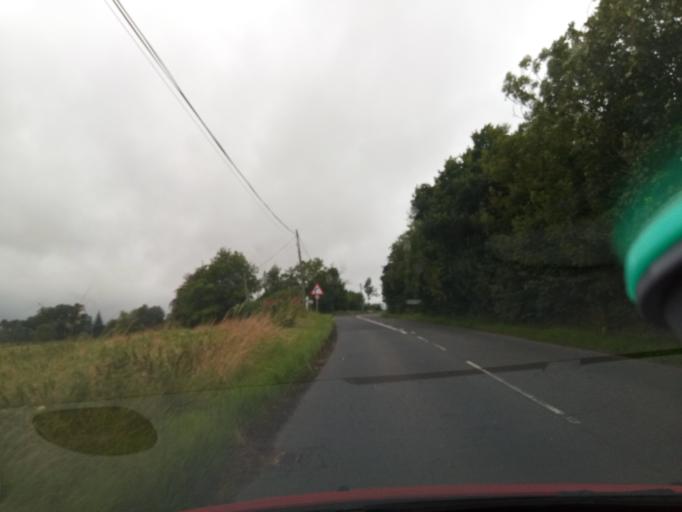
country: GB
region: Scotland
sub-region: The Scottish Borders
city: Kelso
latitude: 55.6288
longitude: -2.5078
